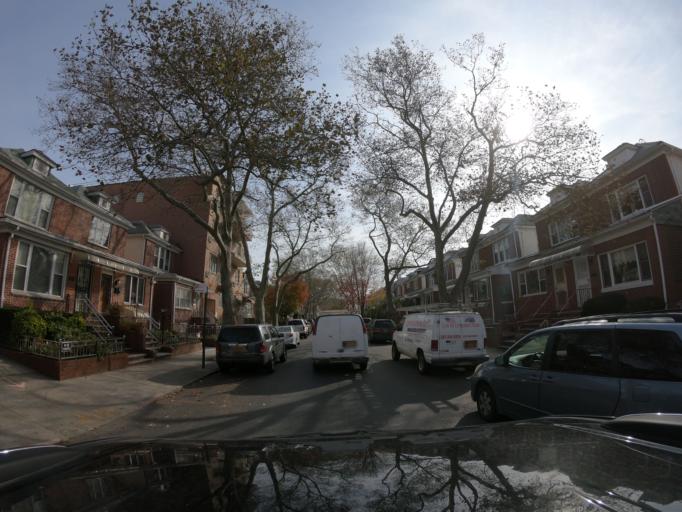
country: US
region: New York
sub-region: Kings County
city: Bensonhurst
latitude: 40.6153
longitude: -73.9791
